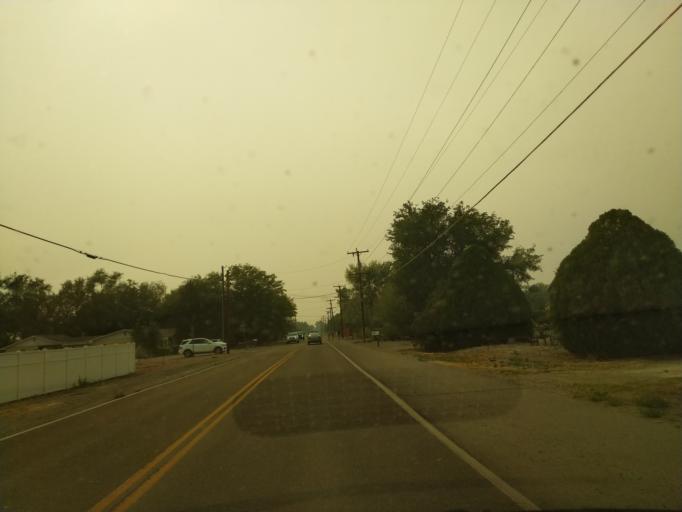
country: US
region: Colorado
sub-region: Mesa County
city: Fruitvale
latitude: 39.0846
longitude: -108.4894
